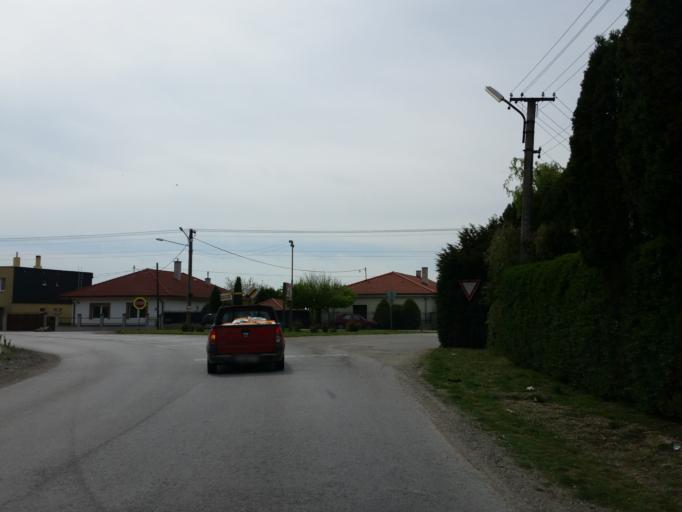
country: SK
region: Trnavsky
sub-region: Okres Dunajska Streda
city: Velky Meder
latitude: 47.9743
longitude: 17.7824
